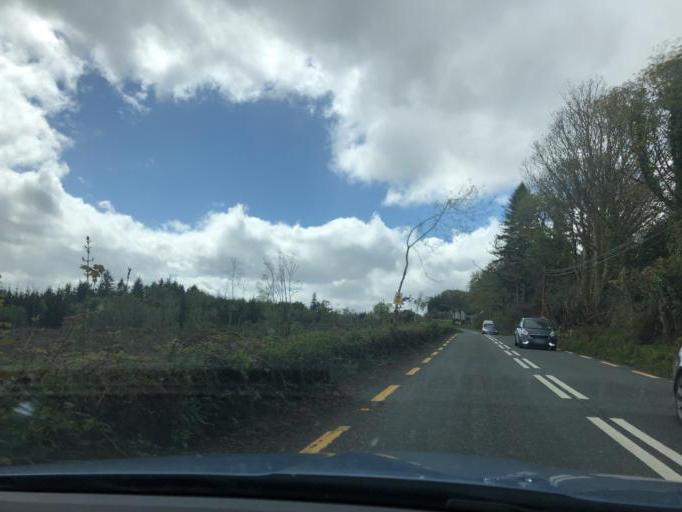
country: IE
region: Munster
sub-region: Ciarrai
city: Kenmare
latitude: 51.8628
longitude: -9.7072
